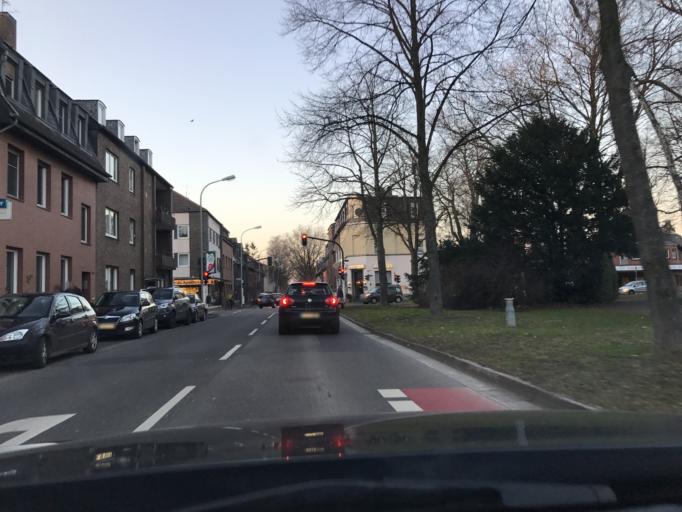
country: DE
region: North Rhine-Westphalia
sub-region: Regierungsbezirk Dusseldorf
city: Krefeld
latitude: 51.3322
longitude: 6.6120
